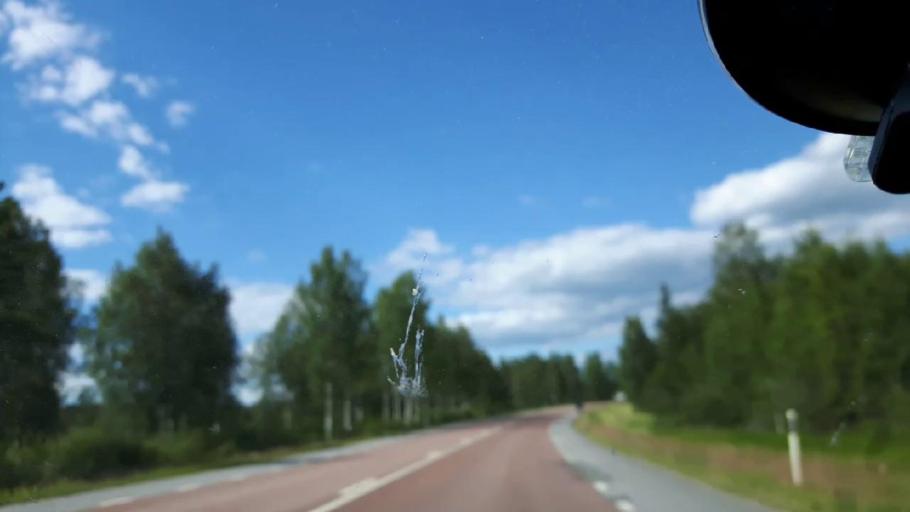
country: SE
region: Jaemtland
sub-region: Braecke Kommun
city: Braecke
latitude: 62.7615
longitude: 15.4092
